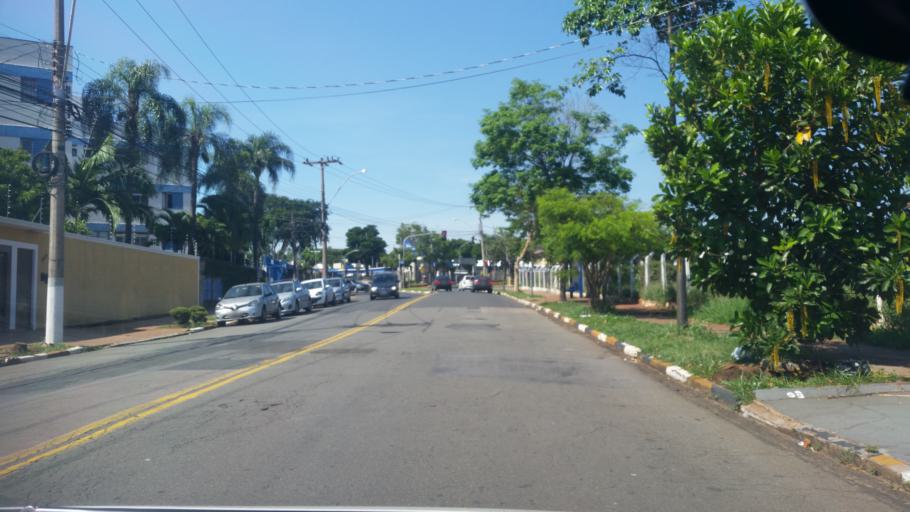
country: BR
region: Sao Paulo
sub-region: Campinas
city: Campinas
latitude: -22.8710
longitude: -47.0648
